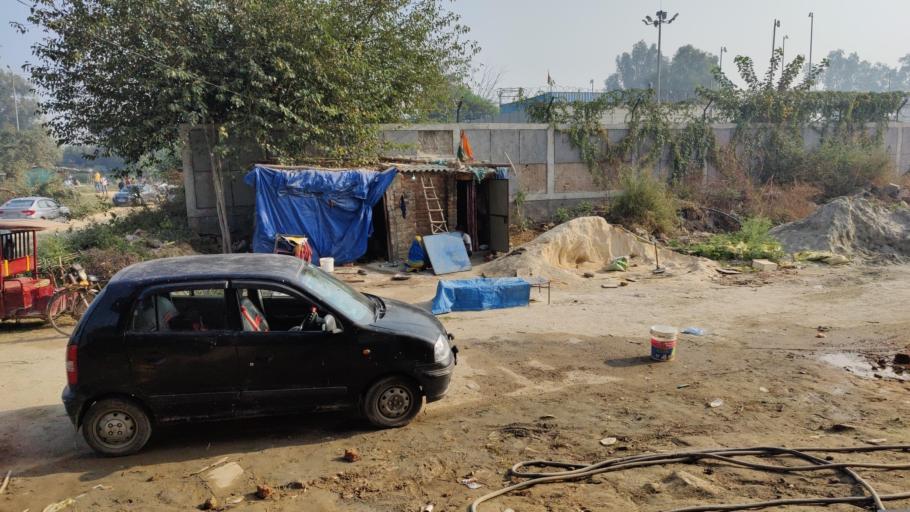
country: IN
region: NCT
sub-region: North West Delhi
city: Alipur
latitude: 28.7650
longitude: 77.1029
